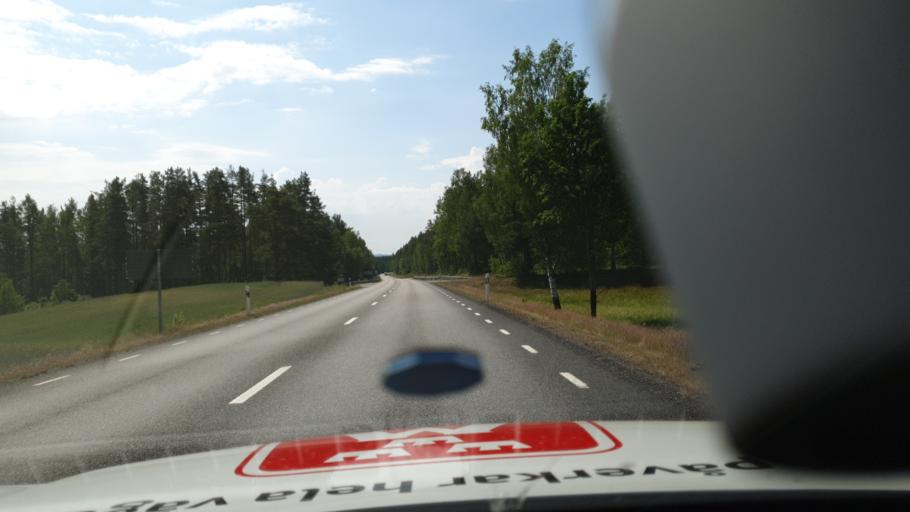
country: SE
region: Joenkoeping
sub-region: Habo Kommun
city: Habo
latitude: 57.9681
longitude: 14.1052
